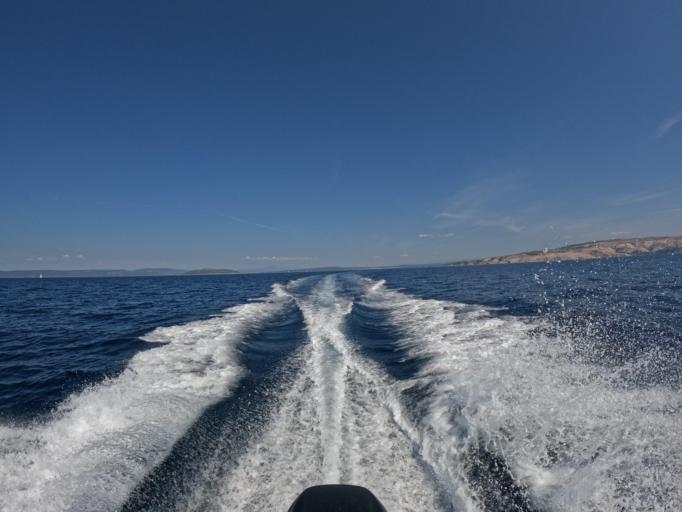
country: HR
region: Primorsko-Goranska
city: Punat
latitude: 44.9085
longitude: 14.6292
